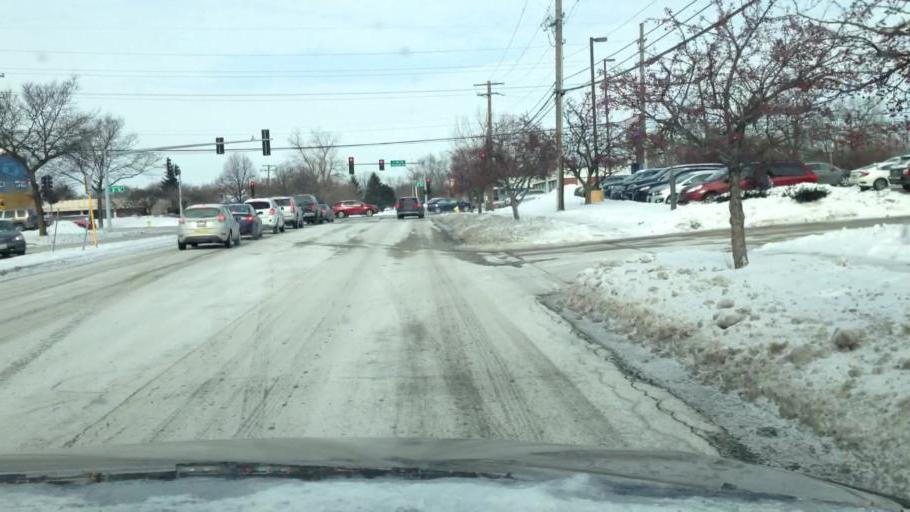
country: US
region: Illinois
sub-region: DuPage County
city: Lombard
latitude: 41.8593
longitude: -88.0122
